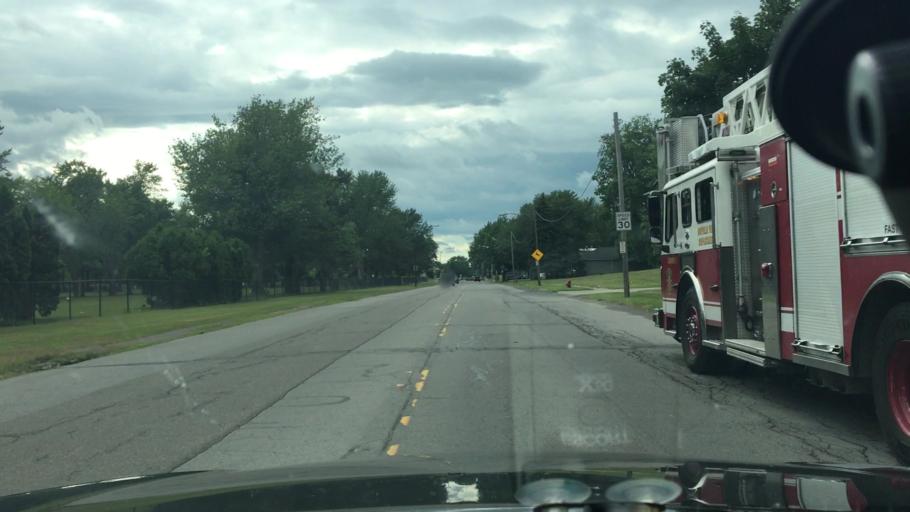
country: US
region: New York
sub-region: Erie County
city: Lackawanna
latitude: 42.8320
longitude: -78.8104
